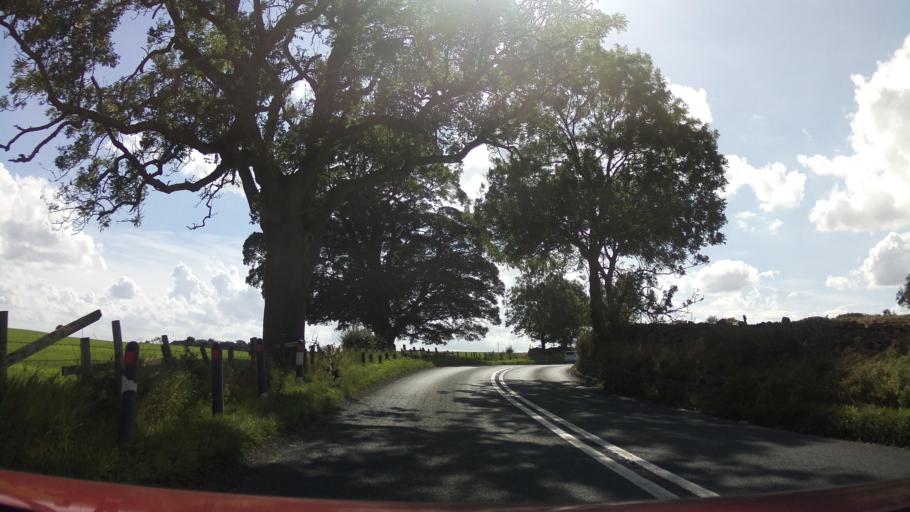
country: GB
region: England
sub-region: North Yorkshire
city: Leyburn
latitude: 54.3472
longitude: -1.8105
